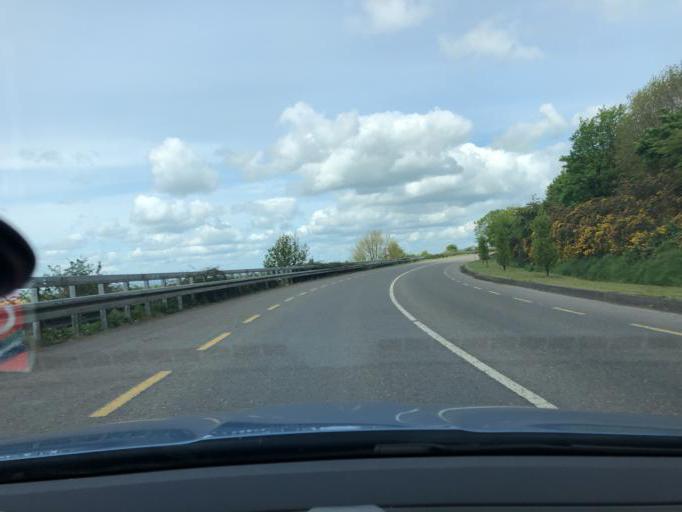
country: IE
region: Munster
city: Cashel
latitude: 52.5228
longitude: -7.8870
